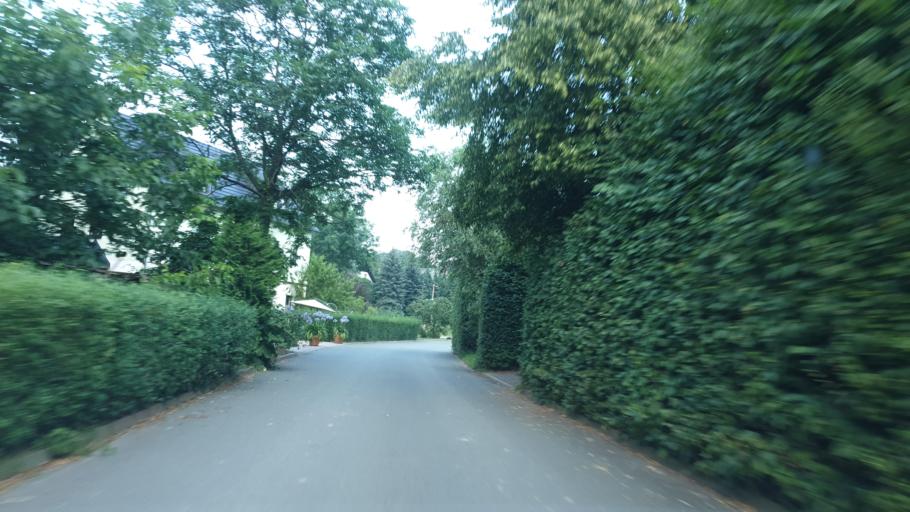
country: DE
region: Saxony
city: Kirchberg
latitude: 50.7671
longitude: 12.7262
